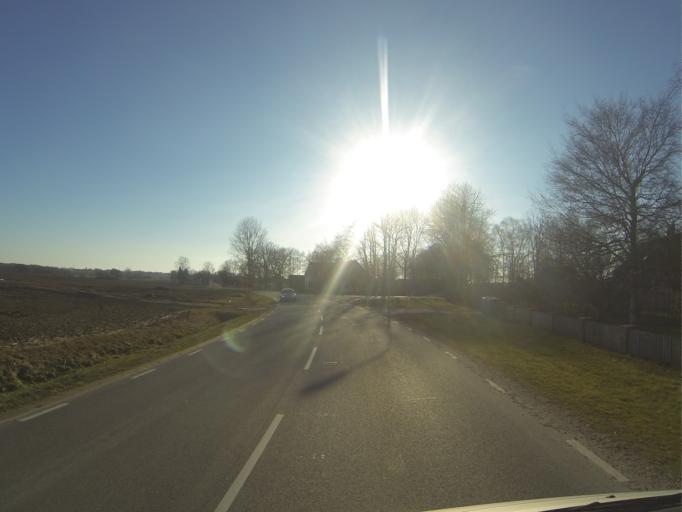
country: SE
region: Skane
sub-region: Horby Kommun
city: Hoerby
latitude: 55.8360
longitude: 13.6191
